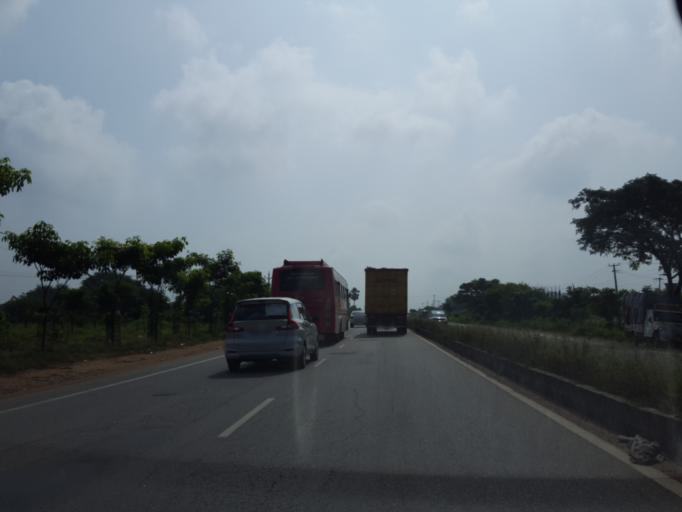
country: IN
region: Telangana
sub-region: Rangareddi
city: Ghatkesar
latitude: 17.2903
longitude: 78.7656
